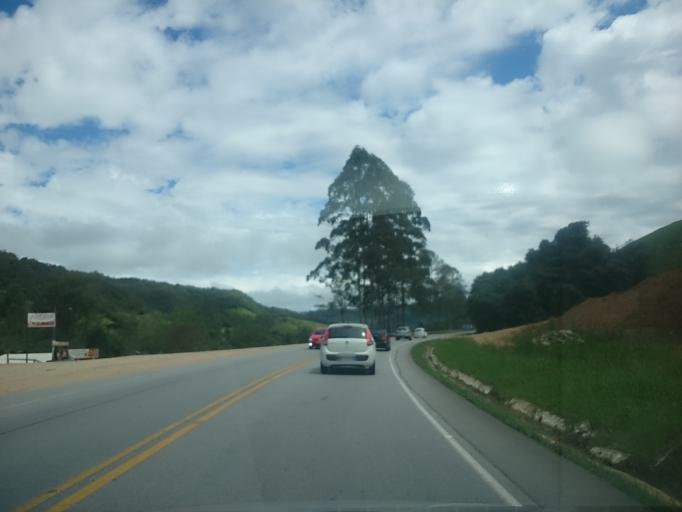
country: BR
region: Santa Catarina
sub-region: Anitapolis
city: Anitapolis
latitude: -27.6888
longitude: -49.2276
